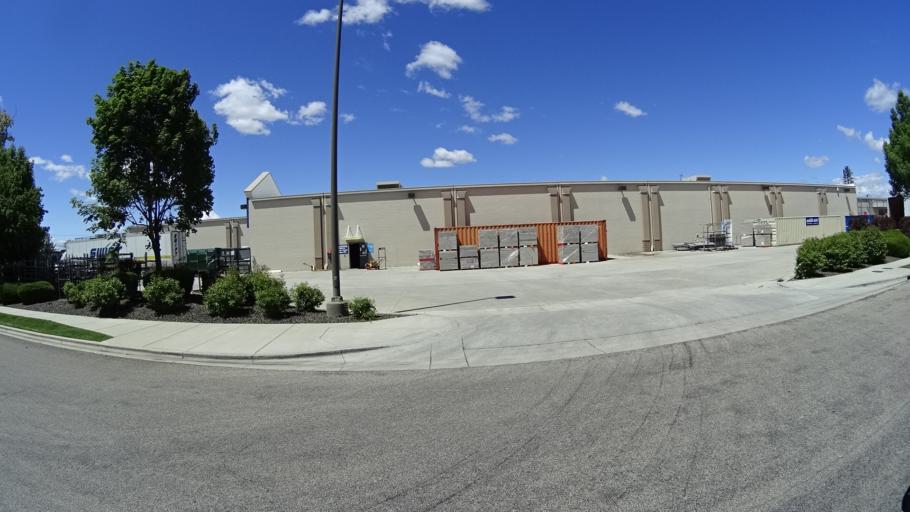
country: US
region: Idaho
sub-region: Ada County
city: Meridian
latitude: 43.6347
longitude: -116.3496
